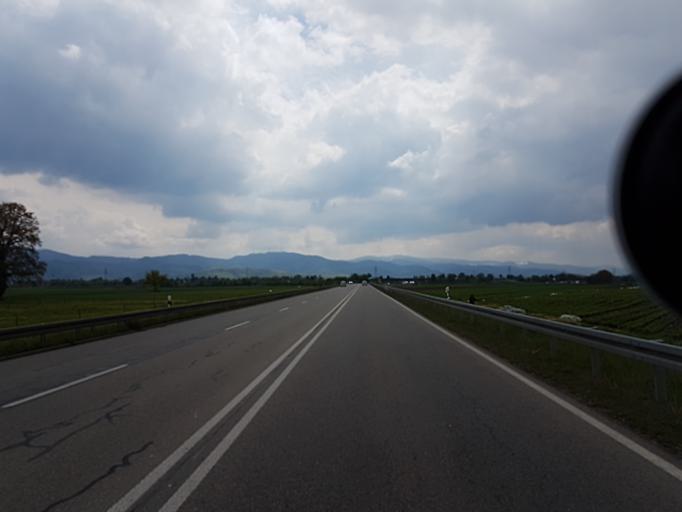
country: DE
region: Baden-Wuerttemberg
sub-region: Freiburg Region
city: Vorstetten
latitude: 48.0812
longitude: 7.8626
